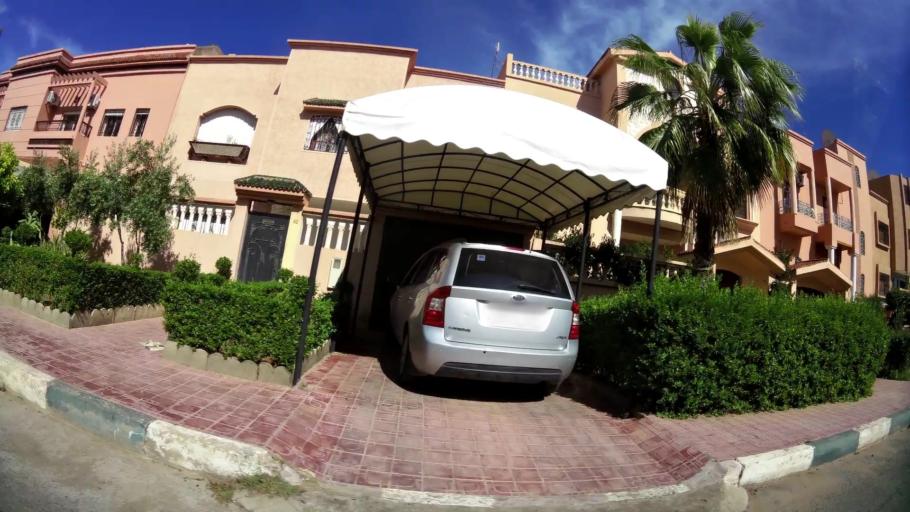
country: MA
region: Marrakech-Tensift-Al Haouz
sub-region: Marrakech
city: Marrakesh
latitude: 31.6556
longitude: -8.0562
